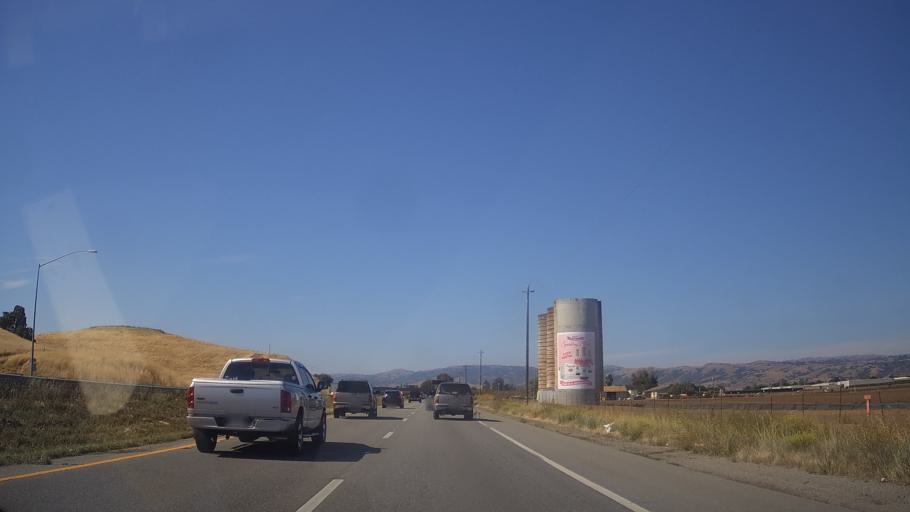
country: US
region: California
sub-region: Santa Clara County
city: Gilroy
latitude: 36.9559
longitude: -121.5504
